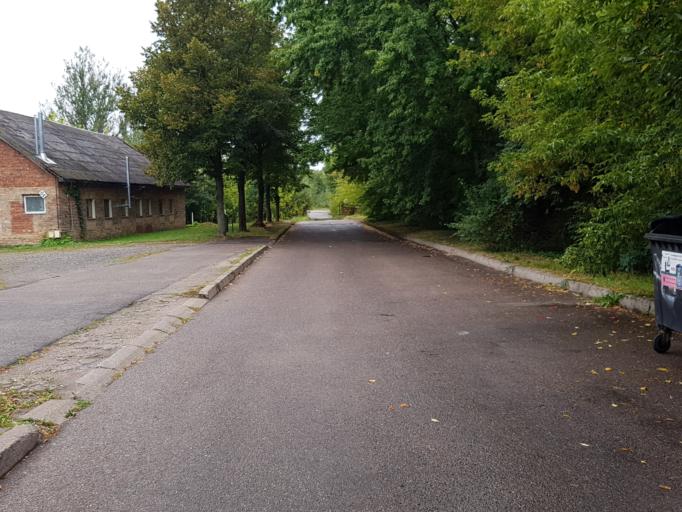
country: LT
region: Vilnius County
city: Lazdynai
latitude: 54.6552
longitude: 25.1948
